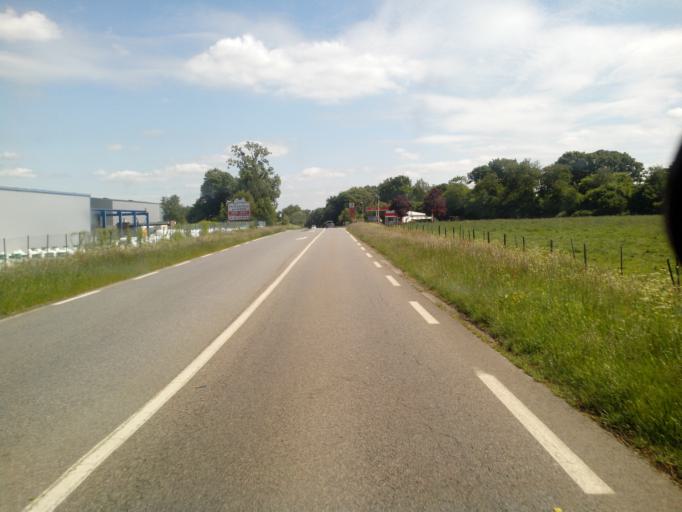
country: FR
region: Haute-Normandie
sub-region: Departement de la Seine-Maritime
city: Tancarville
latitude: 49.4858
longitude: 0.4478
